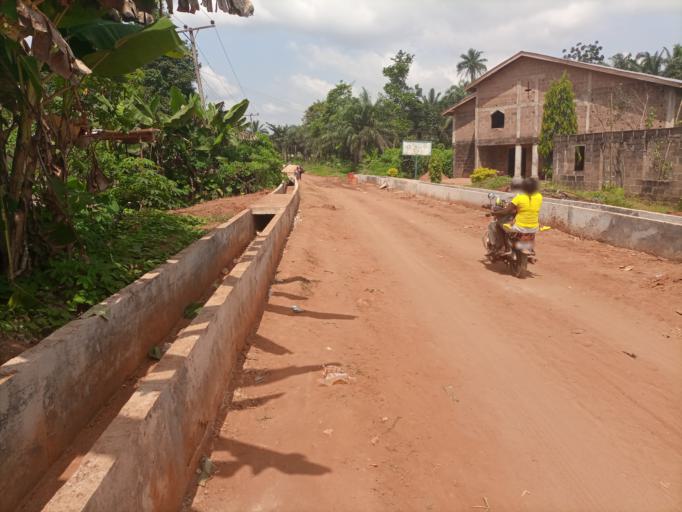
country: NG
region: Imo
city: Ihuo
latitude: 5.5276
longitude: 7.2617
